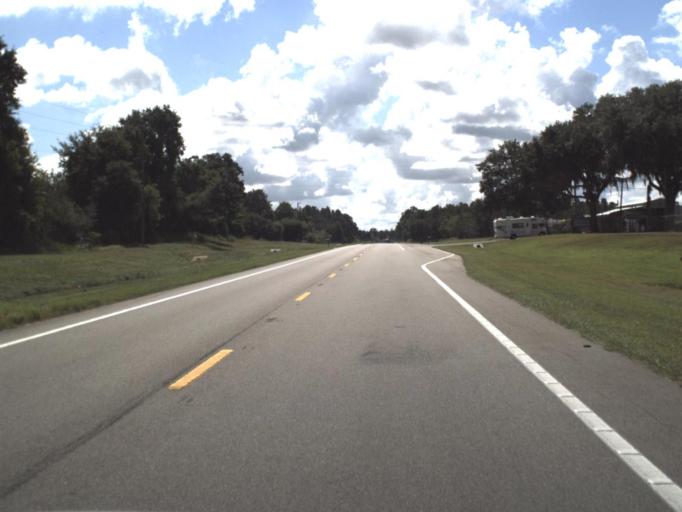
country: US
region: Florida
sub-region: Polk County
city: Kathleen
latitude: 28.2129
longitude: -82.0162
